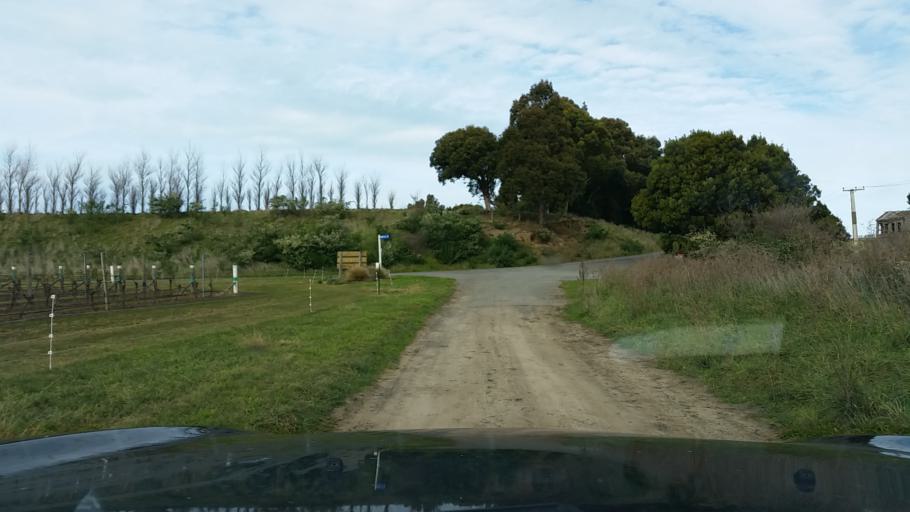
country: NZ
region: Marlborough
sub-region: Marlborough District
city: Blenheim
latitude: -41.6384
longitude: 174.1213
